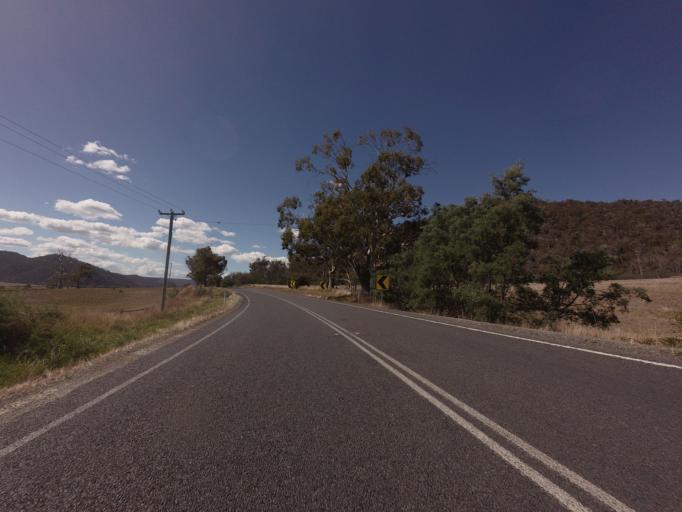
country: AU
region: Tasmania
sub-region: Break O'Day
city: St Helens
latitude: -41.6892
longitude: 147.8794
